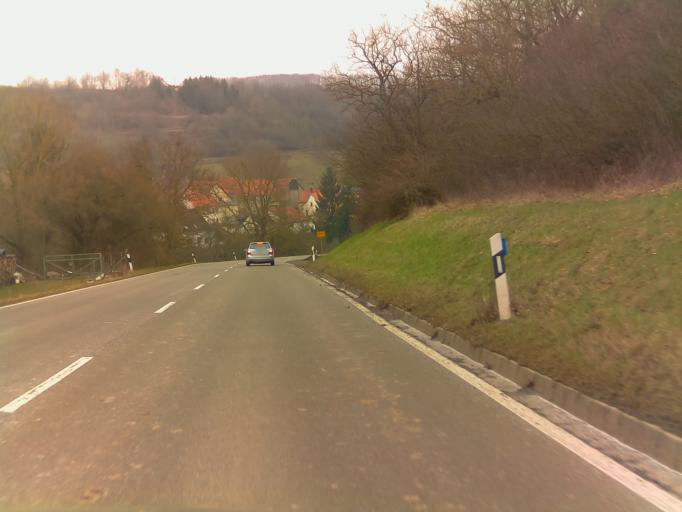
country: DE
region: Rheinland-Pfalz
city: Unkenbach
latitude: 49.7137
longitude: 7.7418
